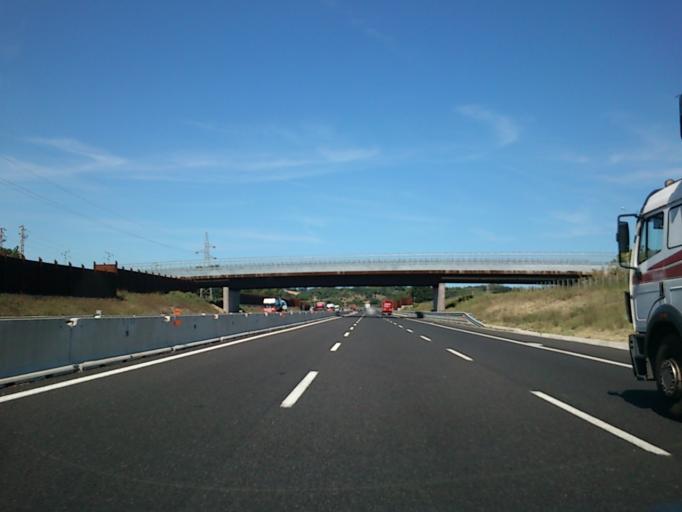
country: IT
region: The Marches
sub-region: Provincia di Pesaro e Urbino
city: Centinarola
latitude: 43.8302
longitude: 12.9956
